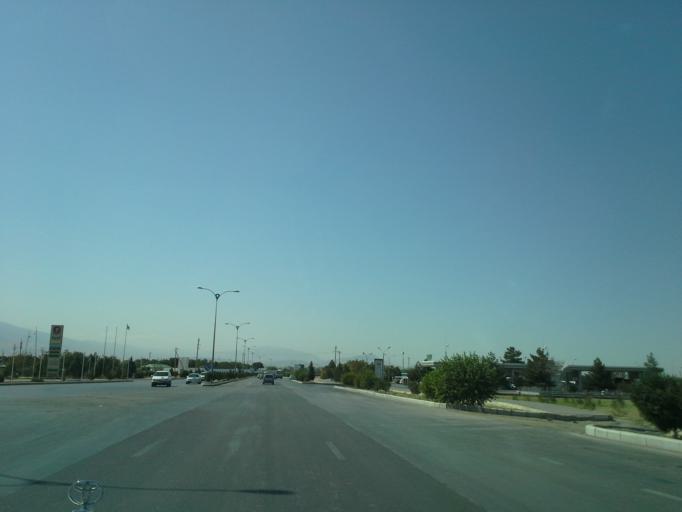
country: TM
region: Ahal
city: Annau
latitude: 37.9073
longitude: 58.5159
